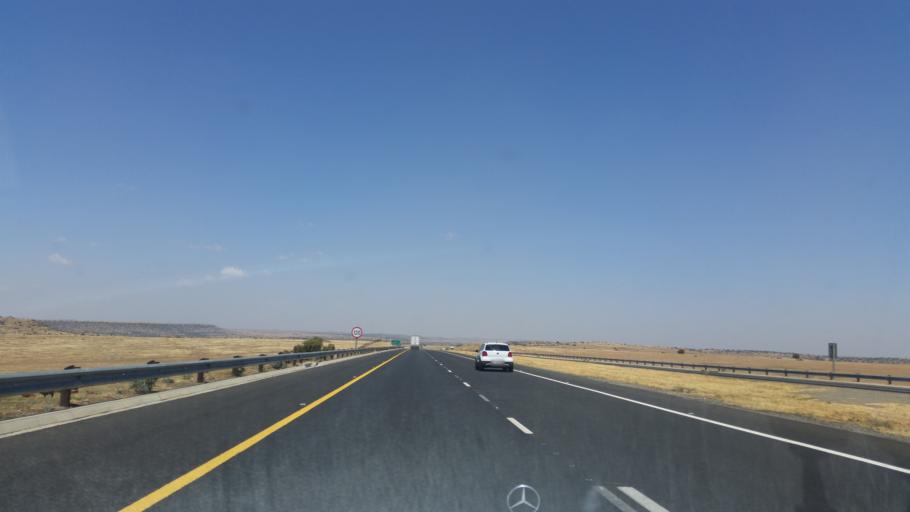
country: ZA
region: Orange Free State
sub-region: Lejweleputswa District Municipality
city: Winburg
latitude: -28.5068
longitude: 26.9946
